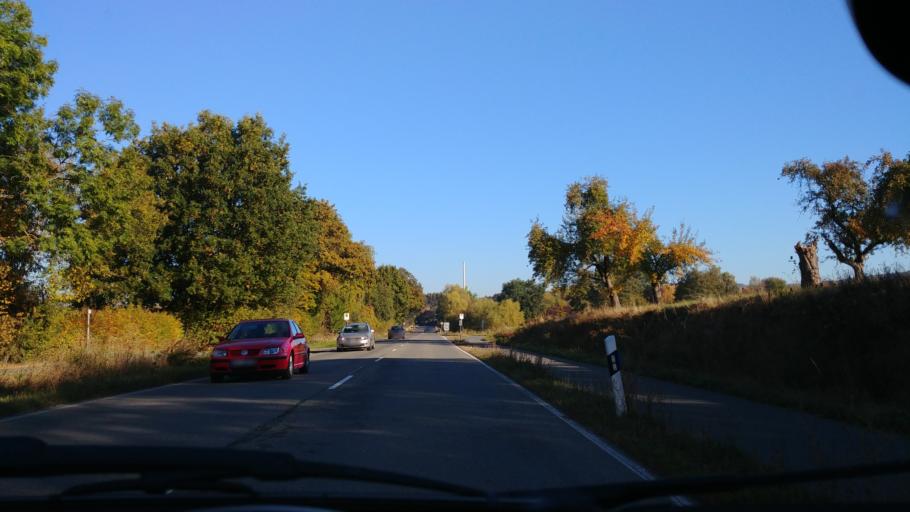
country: DE
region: Rheinland-Pfalz
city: Oelsberg
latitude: 50.2103
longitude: 7.8375
